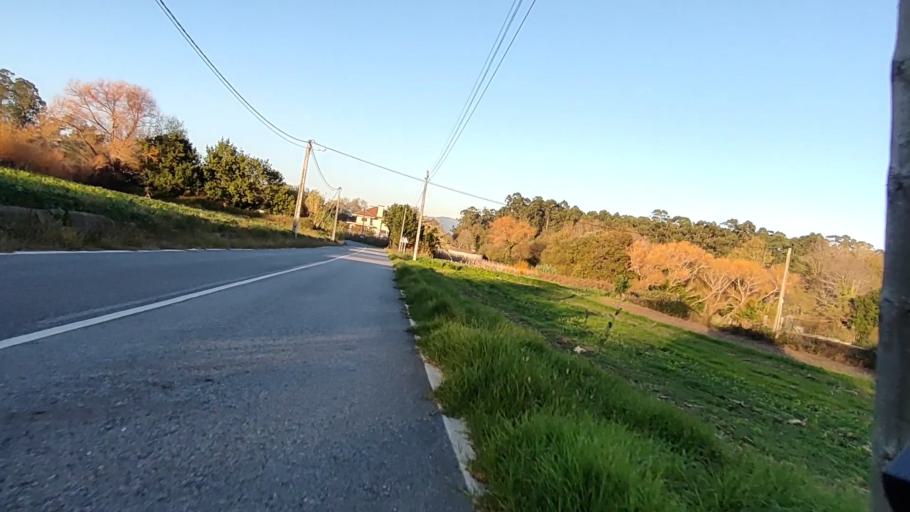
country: ES
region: Galicia
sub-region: Provincia da Coruna
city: Boiro
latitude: 42.6302
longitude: -8.8605
